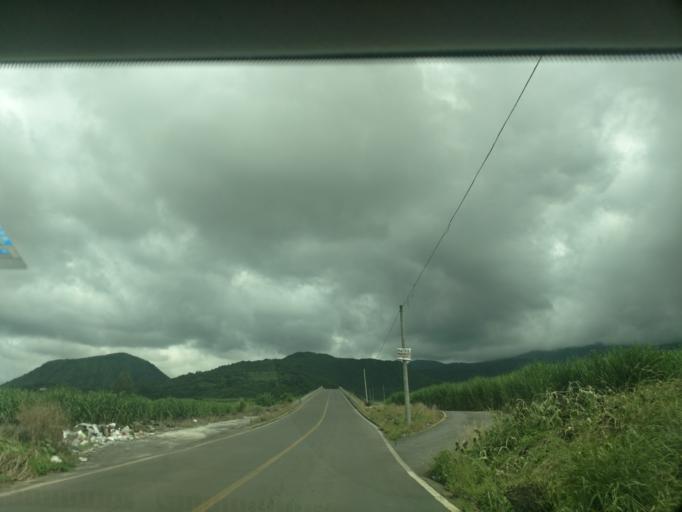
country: MX
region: Nayarit
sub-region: Tepic
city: La Corregidora
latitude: 21.4542
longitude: -104.8066
